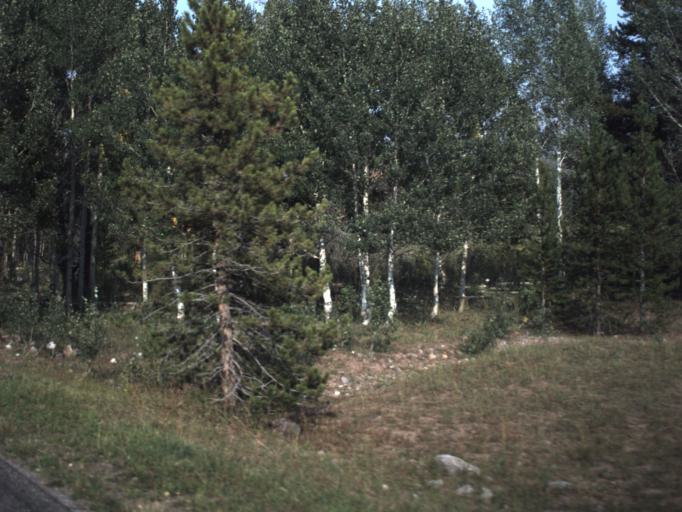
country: US
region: Utah
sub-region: Summit County
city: Oakley
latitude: 40.8169
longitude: -110.8712
